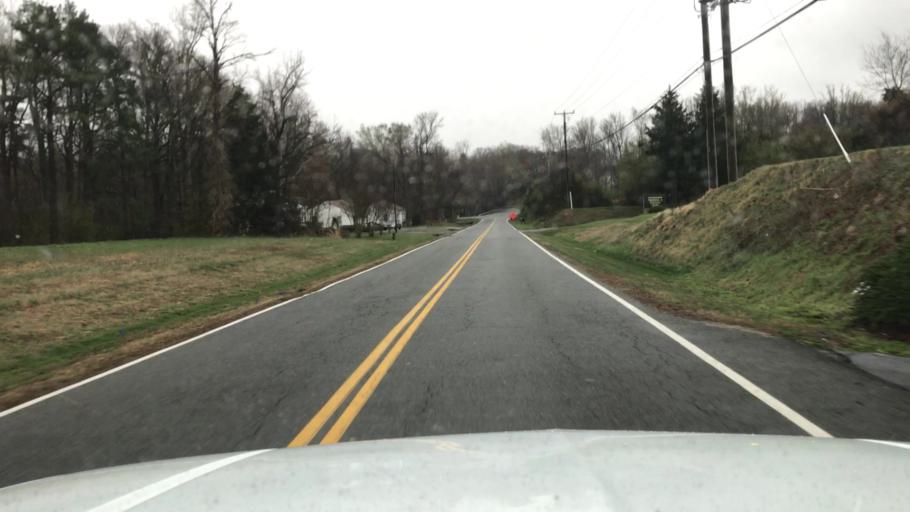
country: US
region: Virginia
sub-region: Henrico County
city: Short Pump
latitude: 37.6677
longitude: -77.6790
